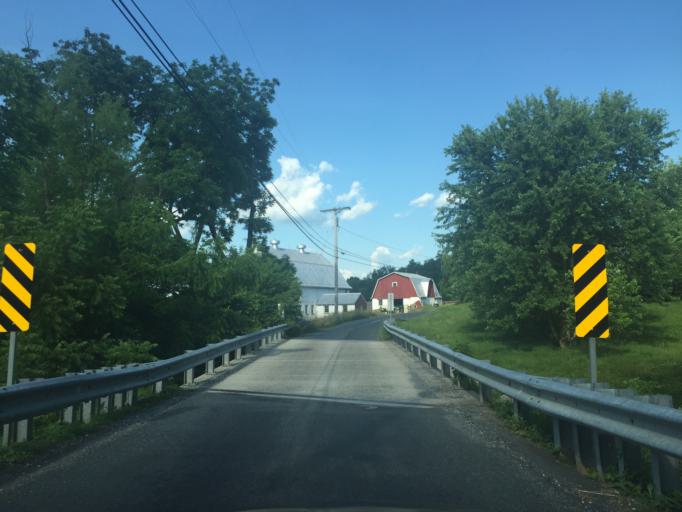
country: US
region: Maryland
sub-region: Harford County
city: Jarrettsville
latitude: 39.6579
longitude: -76.4838
